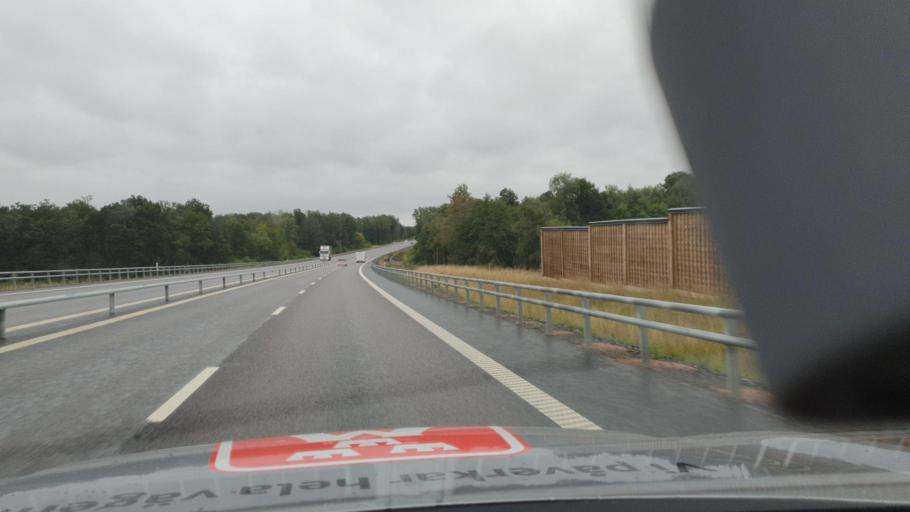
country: SE
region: Skane
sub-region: Hassleholms Kommun
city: Vinslov
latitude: 55.9487
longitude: 13.8975
